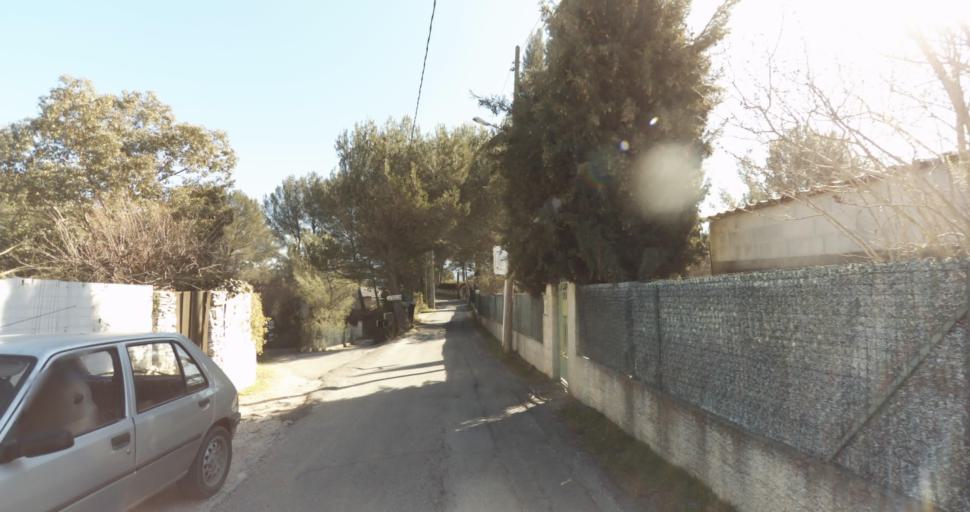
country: FR
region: Provence-Alpes-Cote d'Azur
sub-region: Departement des Bouches-du-Rhone
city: La Bouilladisse
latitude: 43.3883
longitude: 5.5886
